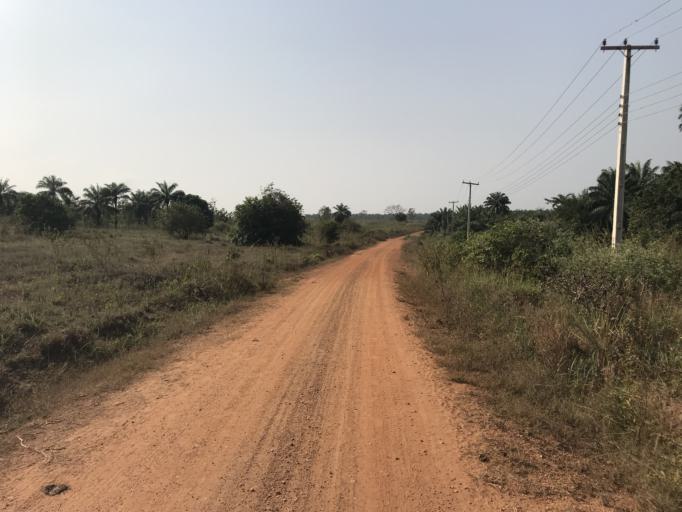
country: NG
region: Osun
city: Olupona
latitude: 7.6028
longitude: 4.1412
